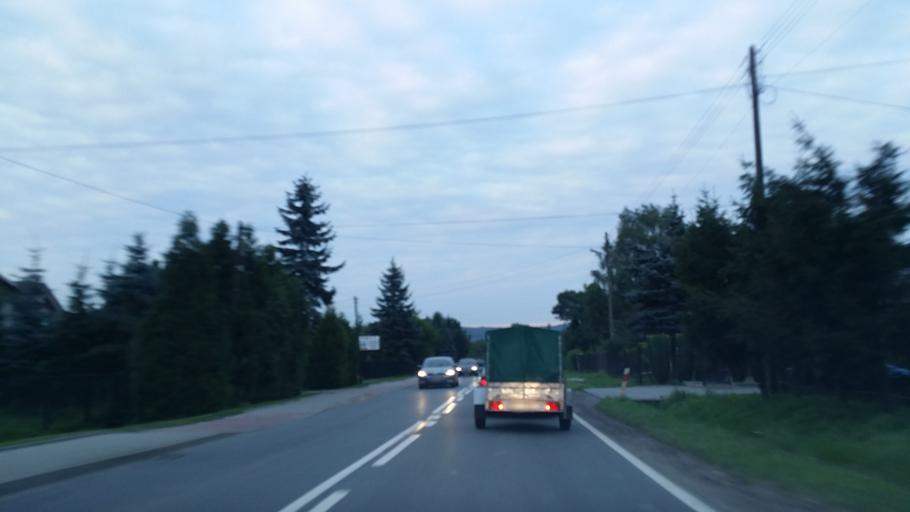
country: PL
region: Lesser Poland Voivodeship
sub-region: Powiat krakowski
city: Liszki
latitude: 50.0391
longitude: 19.7767
